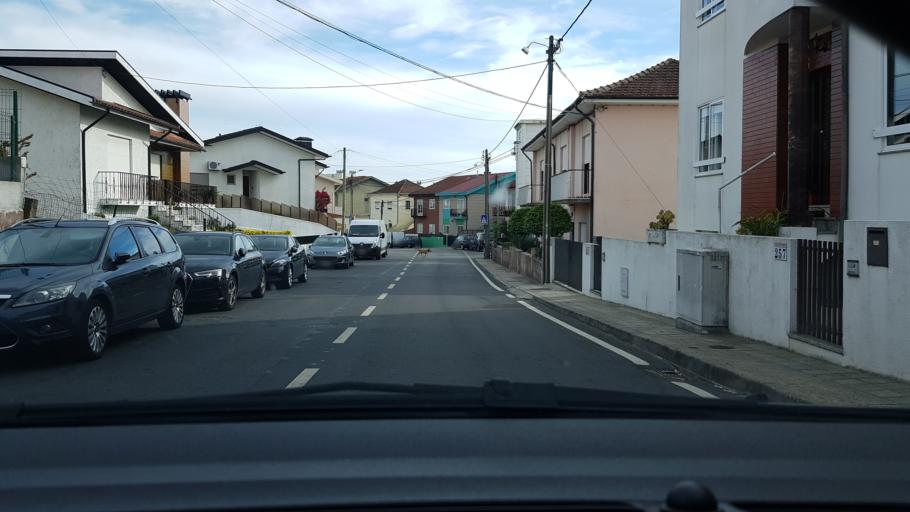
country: PT
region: Porto
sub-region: Gondomar
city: Rio Tinto
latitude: 41.1905
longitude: -8.5535
